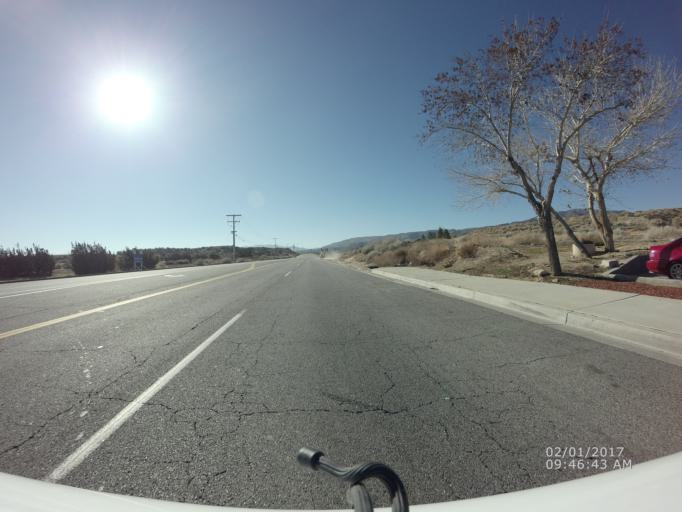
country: US
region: California
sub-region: Los Angeles County
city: Palmdale
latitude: 34.5565
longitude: -118.1143
